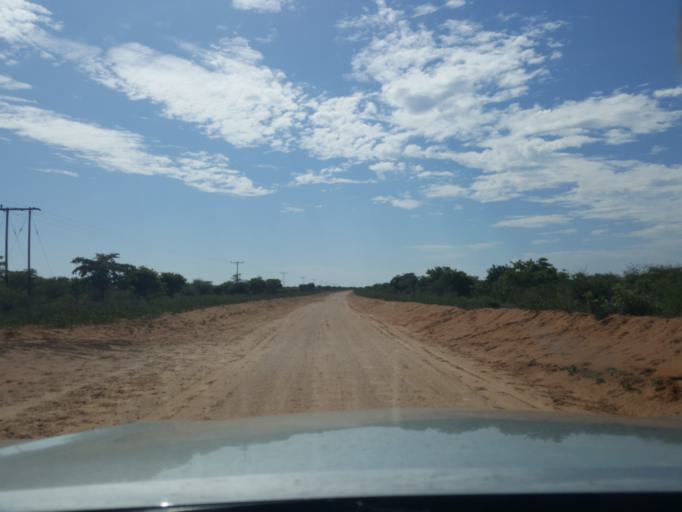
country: BW
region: Kweneng
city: Khudumelapye
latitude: -23.8598
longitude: 24.8831
